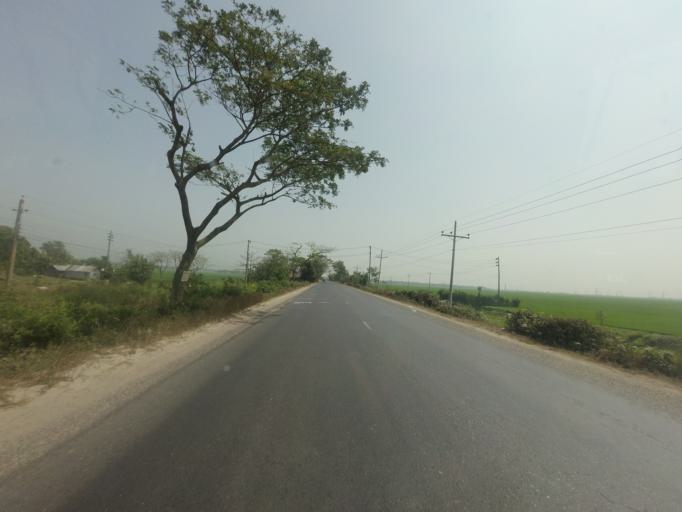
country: BD
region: Dhaka
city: Bhairab Bazar
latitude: 24.0538
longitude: 91.1533
